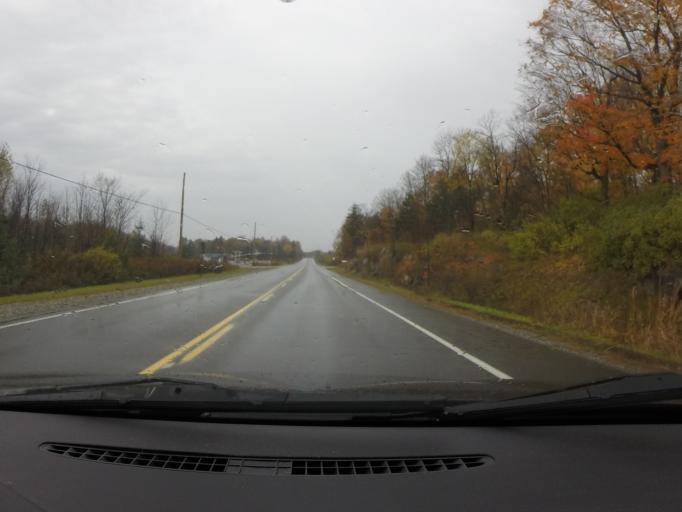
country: CA
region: Ontario
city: Perth
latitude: 44.8297
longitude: -76.5751
